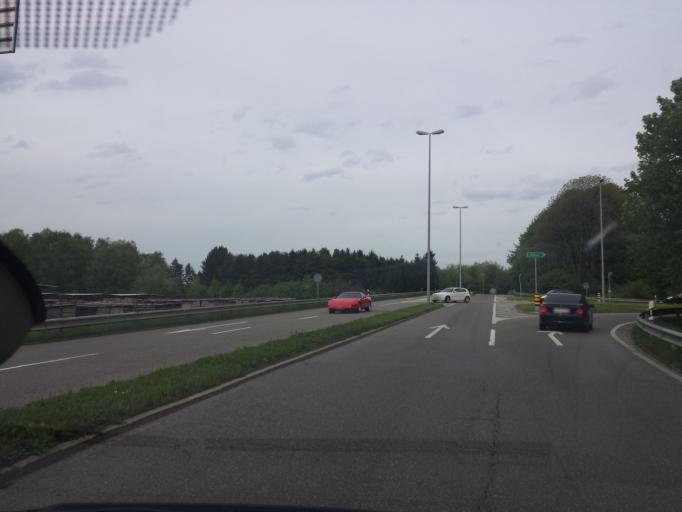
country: AT
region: Vorarlberg
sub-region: Politischer Bezirk Bregenz
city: Hochst
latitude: 47.4522
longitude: 9.6492
